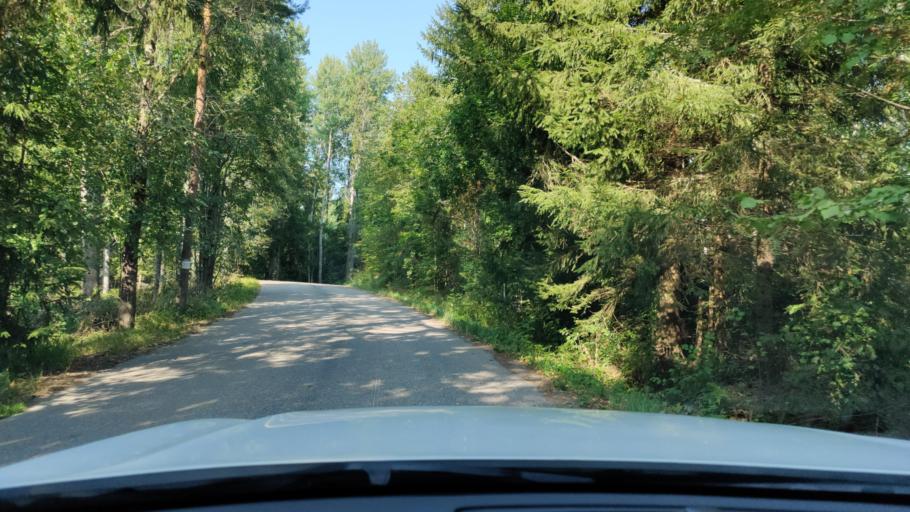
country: FI
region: Haeme
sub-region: Haemeenlinna
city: Tervakoski
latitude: 60.6735
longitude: 24.6367
